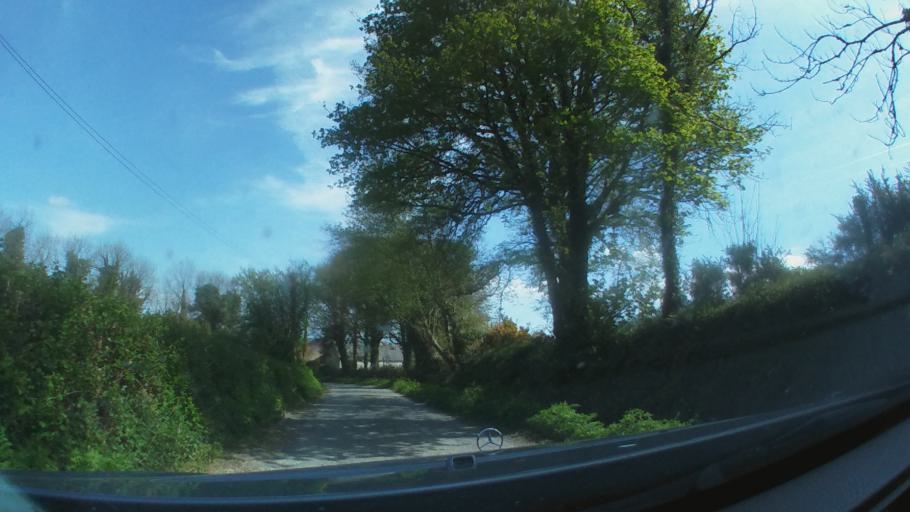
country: IE
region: Leinster
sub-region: Kilkenny
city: Callan
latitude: 52.6218
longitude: -7.5115
